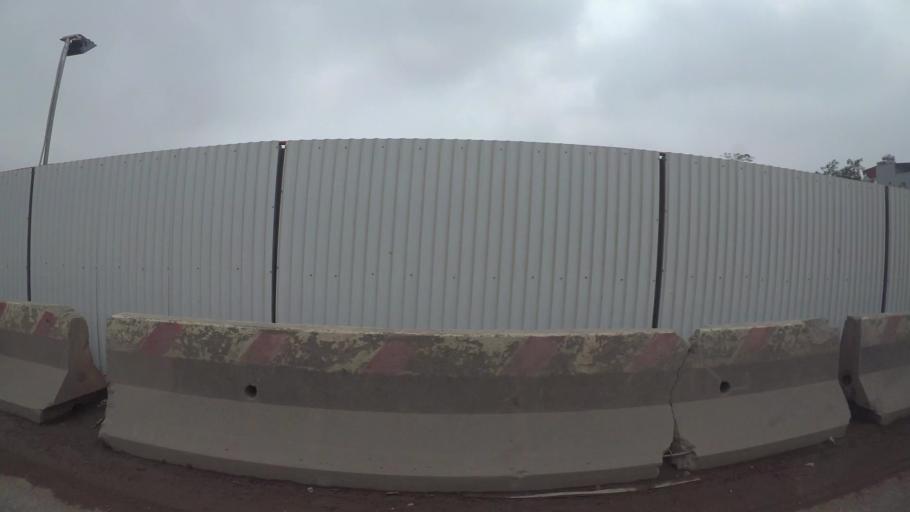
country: VN
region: Ha Noi
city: Tay Ho
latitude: 21.0753
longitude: 105.7858
